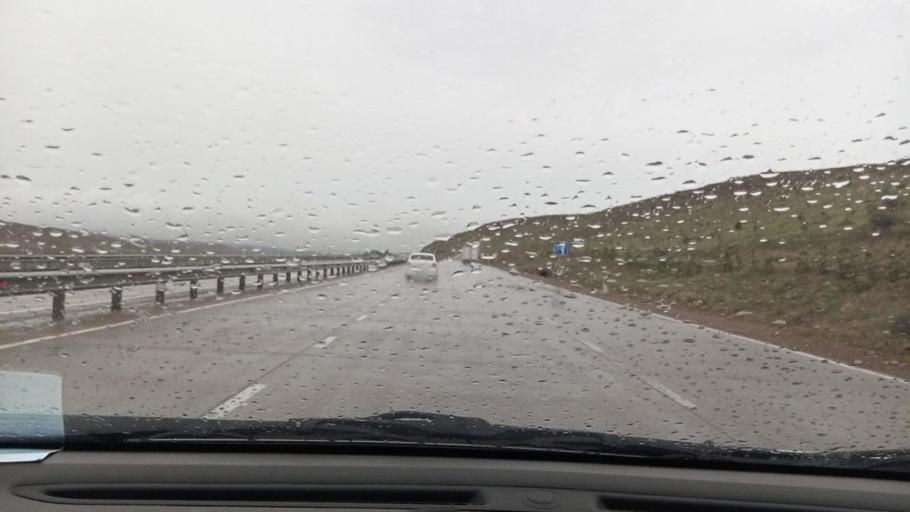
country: UZ
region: Namangan
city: Pop Shahri
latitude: 40.9272
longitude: 70.7178
